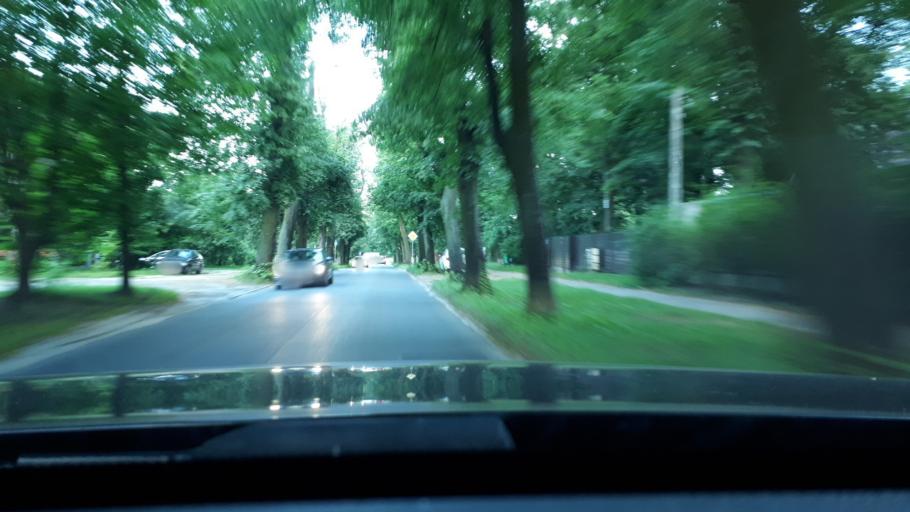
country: PL
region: Masovian Voivodeship
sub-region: Powiat pruszkowski
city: Komorow
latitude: 52.1454
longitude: 20.8243
